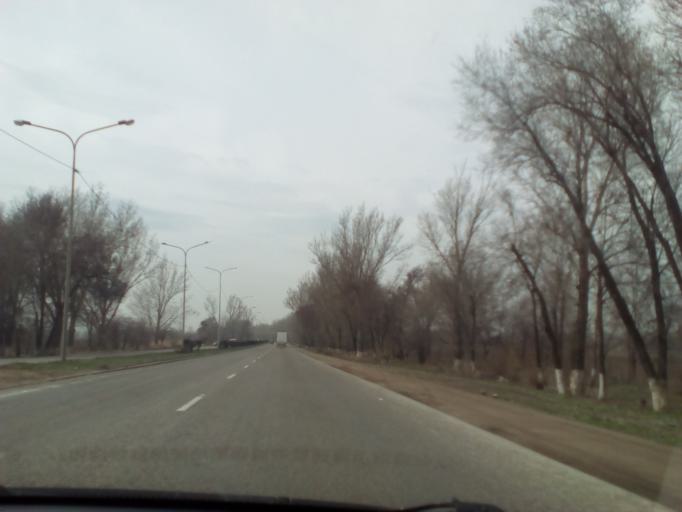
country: KZ
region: Almaty Oblysy
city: Burunday
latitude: 43.2225
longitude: 76.6163
